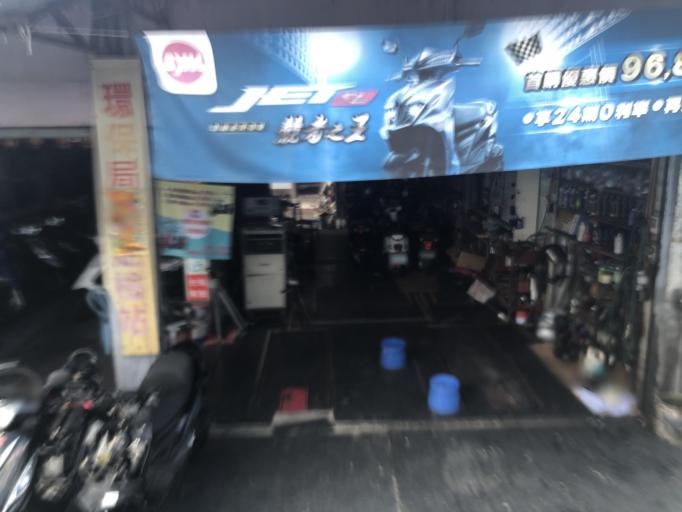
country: TW
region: Taiwan
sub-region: Pingtung
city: Pingtung
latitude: 22.8973
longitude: 120.5492
